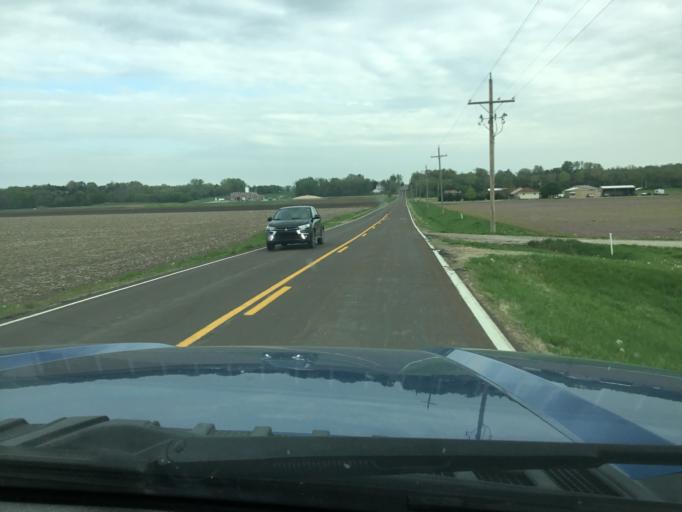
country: US
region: Kansas
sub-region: Shawnee County
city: Topeka
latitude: 39.0989
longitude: -95.7483
